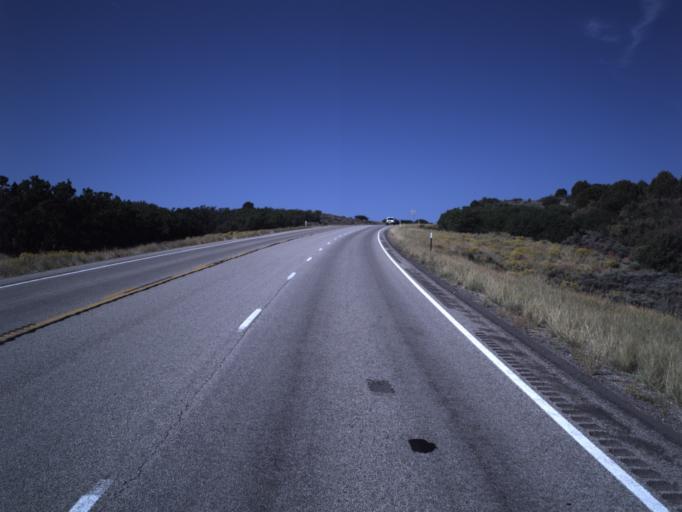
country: US
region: Utah
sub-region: San Juan County
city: Monticello
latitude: 37.7733
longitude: -109.3587
